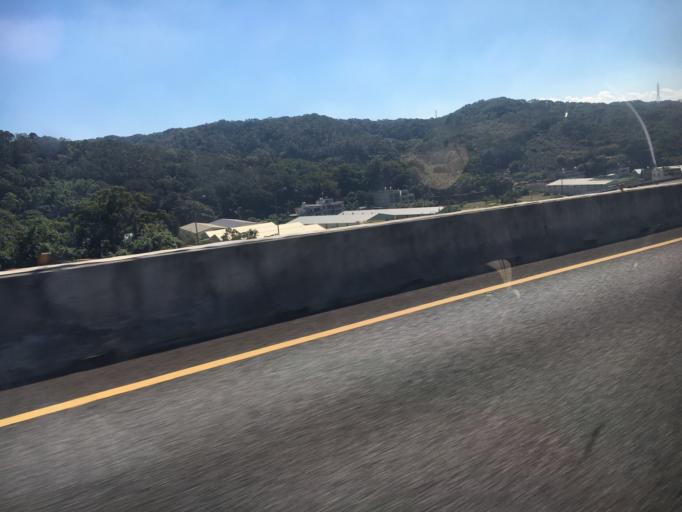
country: TW
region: Taiwan
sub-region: Taoyuan
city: Taoyuan
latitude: 25.0552
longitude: 121.3275
